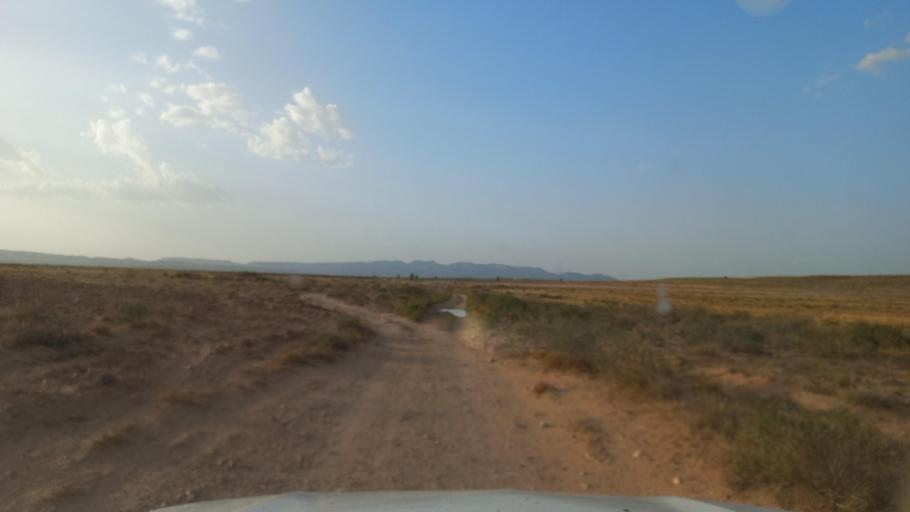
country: TN
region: Al Qasrayn
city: Sbiba
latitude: 35.3065
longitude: 9.0743
